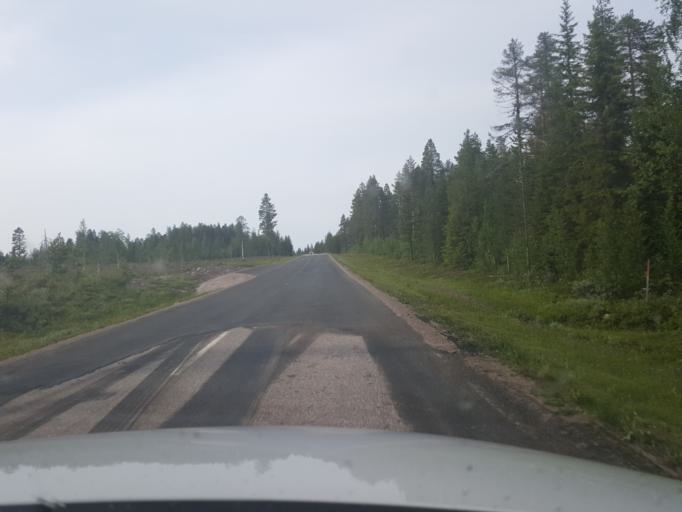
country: SE
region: Norrbotten
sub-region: Arjeplogs Kommun
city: Arjeplog
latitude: 65.7639
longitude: 18.0230
